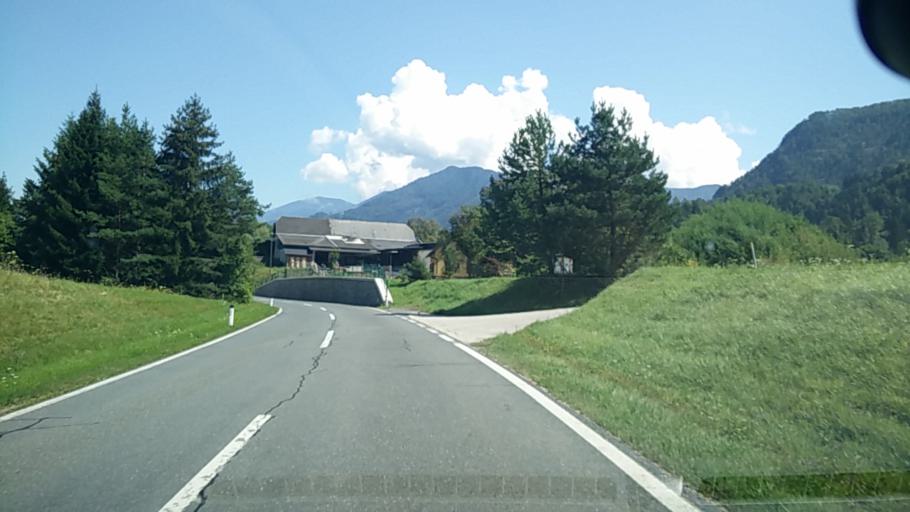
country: AT
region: Carinthia
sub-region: Politischer Bezirk Volkermarkt
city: Gallizien
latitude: 46.5397
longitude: 14.5551
